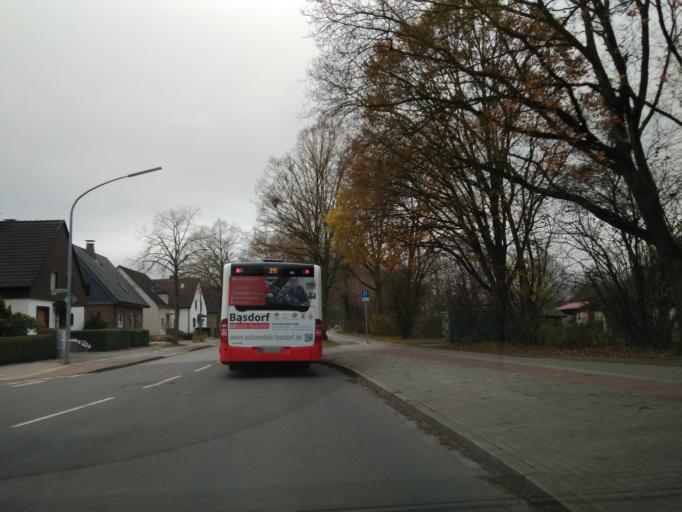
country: DE
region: North Rhine-Westphalia
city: Marl
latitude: 51.6025
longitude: 7.0620
